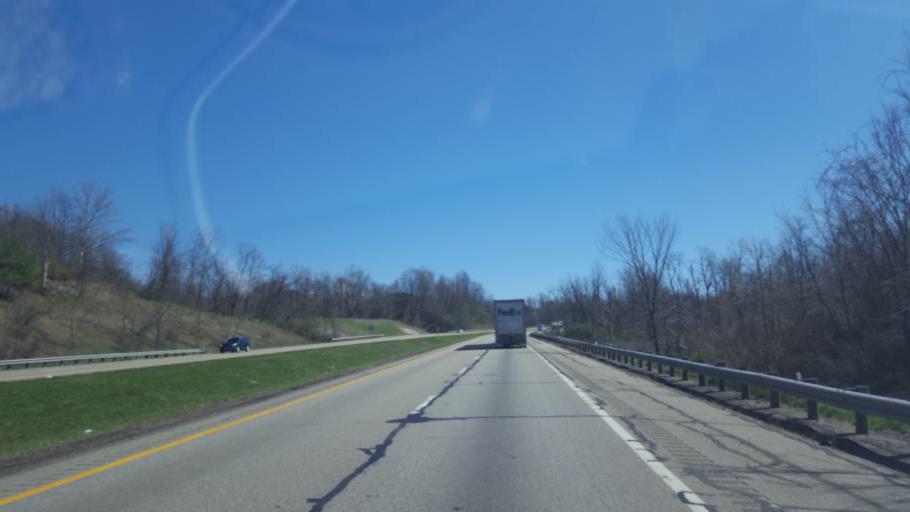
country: US
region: Ohio
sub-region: Belmont County
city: Bethesda
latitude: 40.0583
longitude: -81.1069
